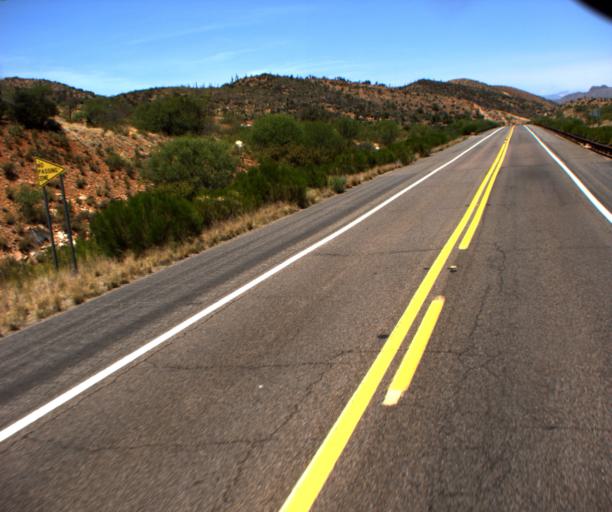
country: US
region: Arizona
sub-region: Gila County
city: Claypool
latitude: 33.4974
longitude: -110.8660
